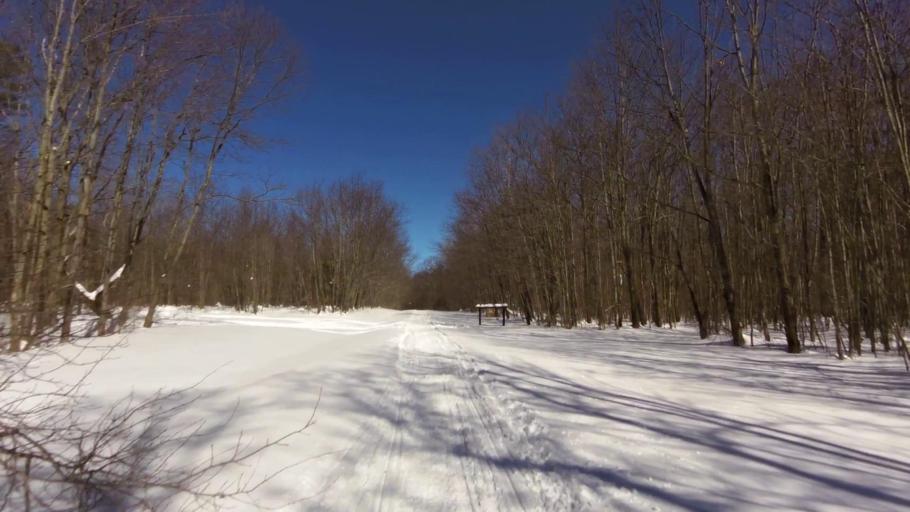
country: US
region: New York
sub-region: Allegany County
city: Cuba
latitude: 42.3195
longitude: -78.2310
